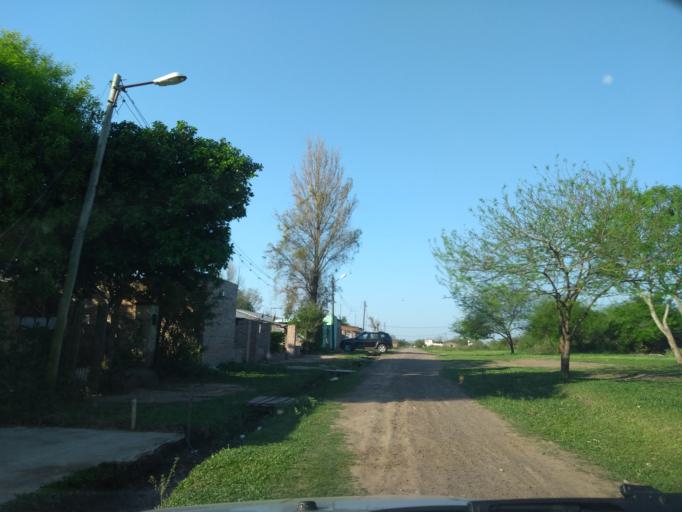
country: AR
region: Chaco
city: Fontana
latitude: -27.4166
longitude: -59.0598
